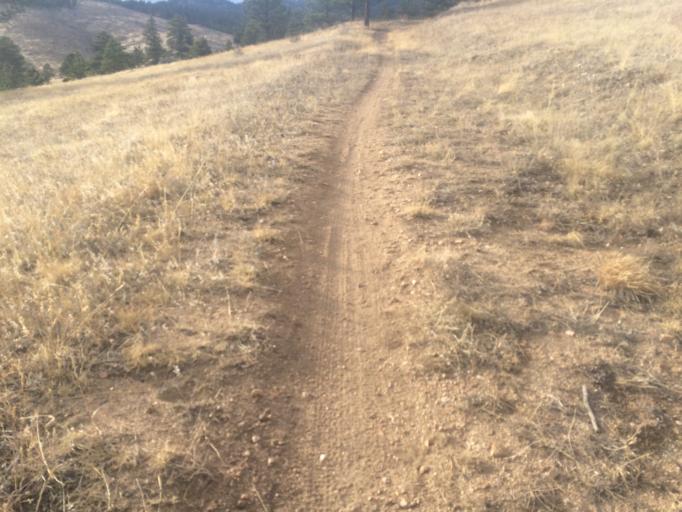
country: US
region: Colorado
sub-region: Boulder County
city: Coal Creek
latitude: 39.9556
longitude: -105.3403
